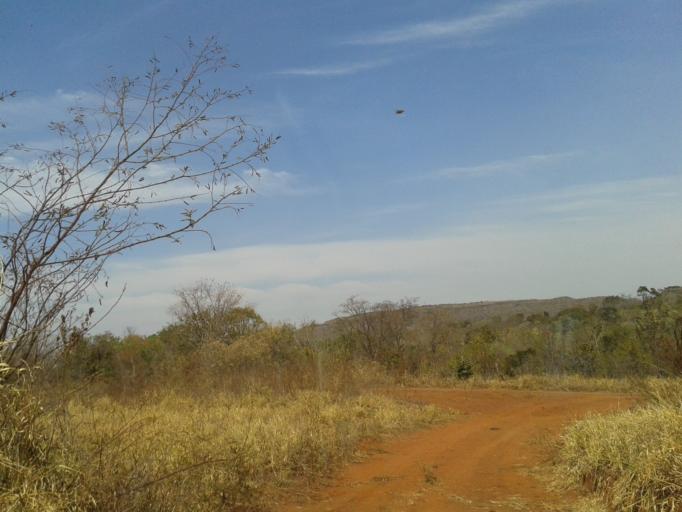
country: BR
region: Minas Gerais
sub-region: Santa Vitoria
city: Santa Vitoria
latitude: -19.2069
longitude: -50.0348
